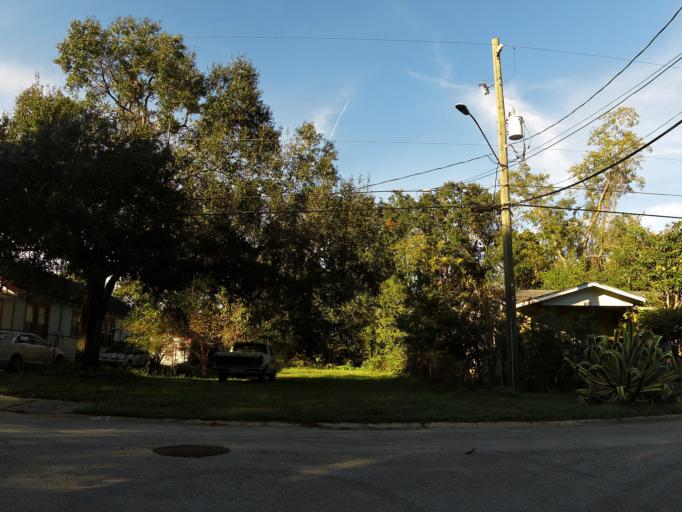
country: US
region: Florida
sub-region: Duval County
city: Jacksonville
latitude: 30.3547
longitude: -81.6916
